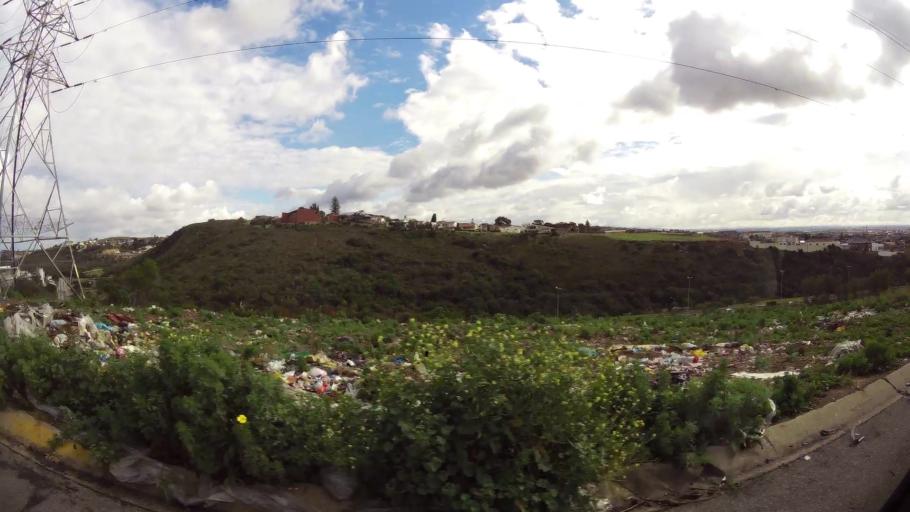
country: ZA
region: Eastern Cape
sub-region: Nelson Mandela Bay Metropolitan Municipality
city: Port Elizabeth
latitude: -33.9291
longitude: 25.5599
